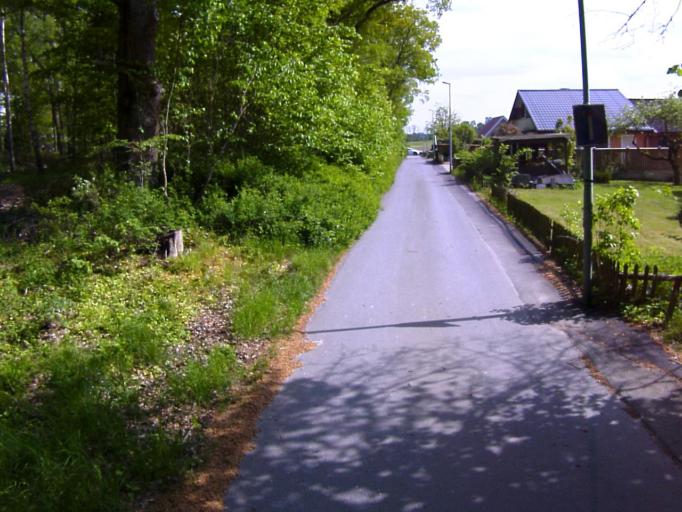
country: SE
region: Skane
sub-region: Kristianstads Kommun
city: Kristianstad
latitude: 56.0558
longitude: 14.0918
